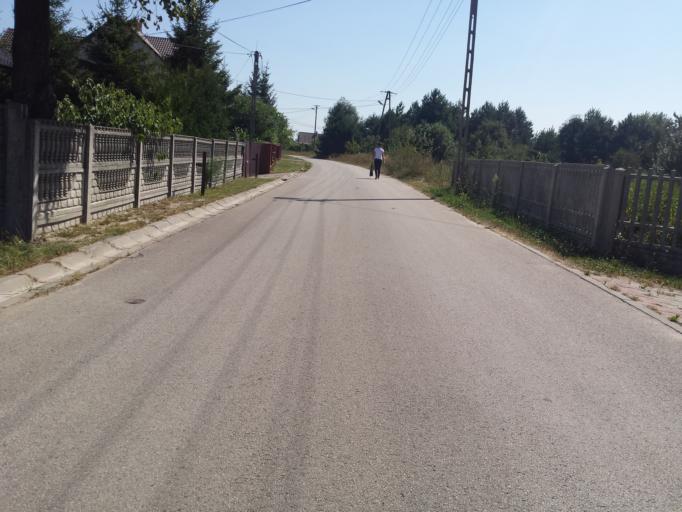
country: PL
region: Swietokrzyskie
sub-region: Powiat kielecki
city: Daleszyce
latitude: 50.8117
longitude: 20.7722
